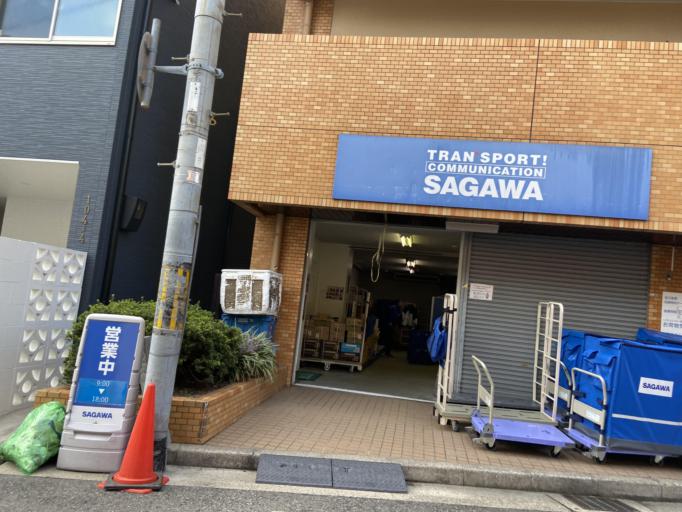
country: JP
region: Hyogo
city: Amagasaki
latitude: 34.7199
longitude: 135.4114
